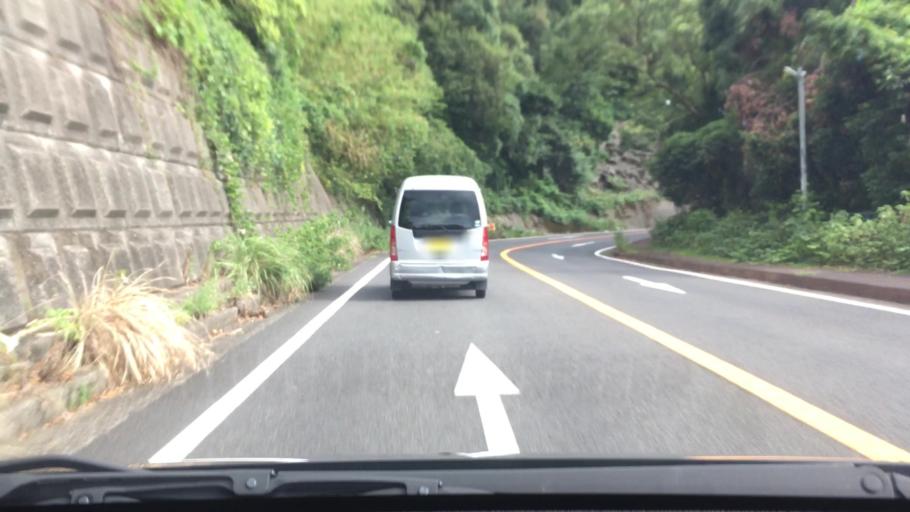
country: JP
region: Nagasaki
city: Togitsu
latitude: 32.8408
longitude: 129.7061
